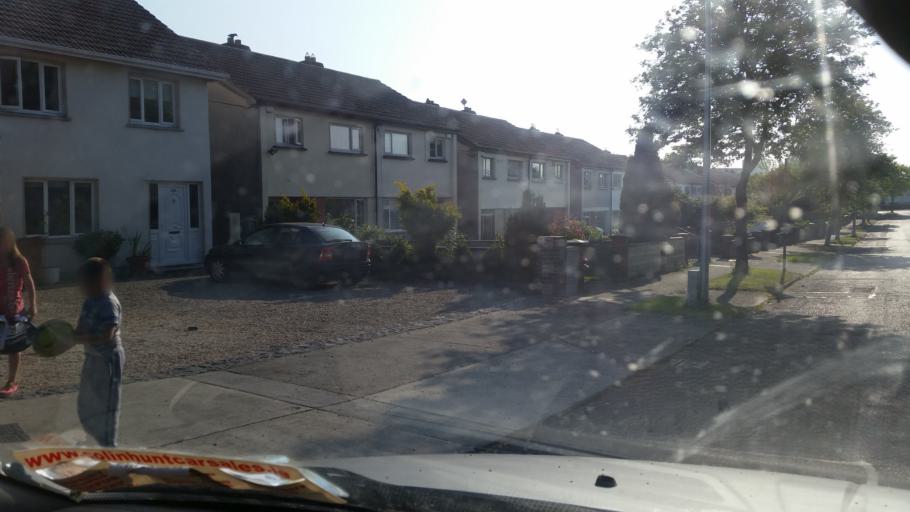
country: IE
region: Leinster
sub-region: Fingal County
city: Blanchardstown
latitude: 53.3957
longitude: -6.3782
